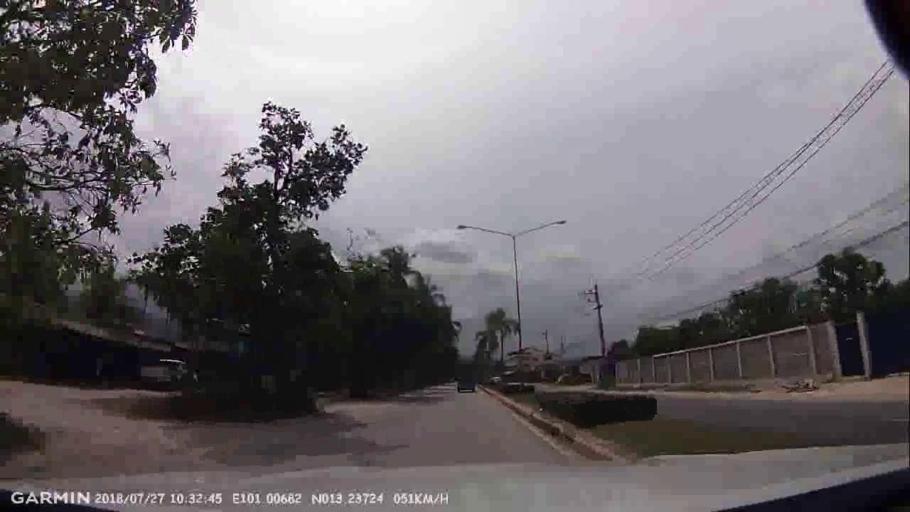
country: TH
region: Chon Buri
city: Si Racha
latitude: 13.2372
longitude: 101.0070
